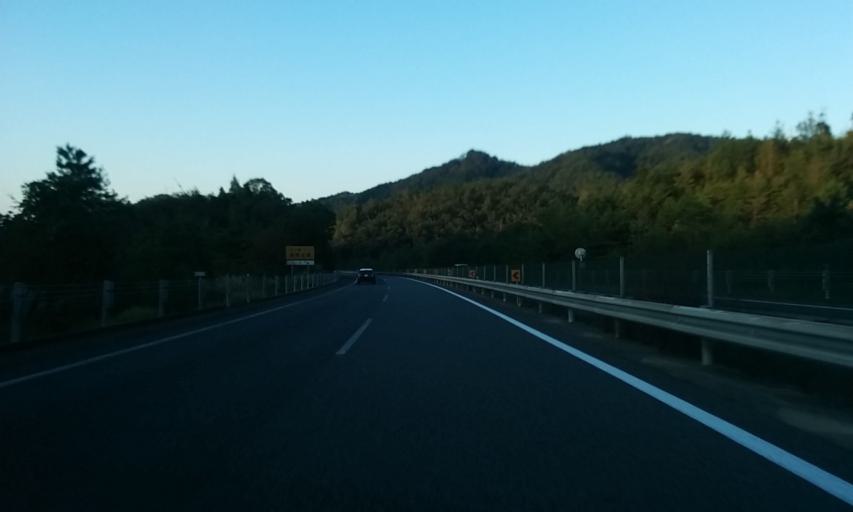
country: JP
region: Kyoto
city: Ayabe
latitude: 35.2289
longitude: 135.1881
